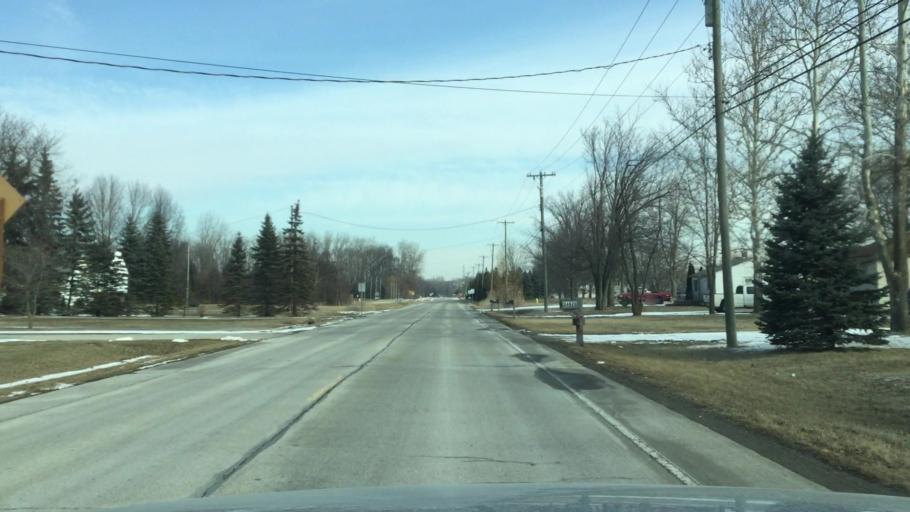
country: US
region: Michigan
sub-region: Wayne County
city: Flat Rock
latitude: 42.1263
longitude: -83.2898
